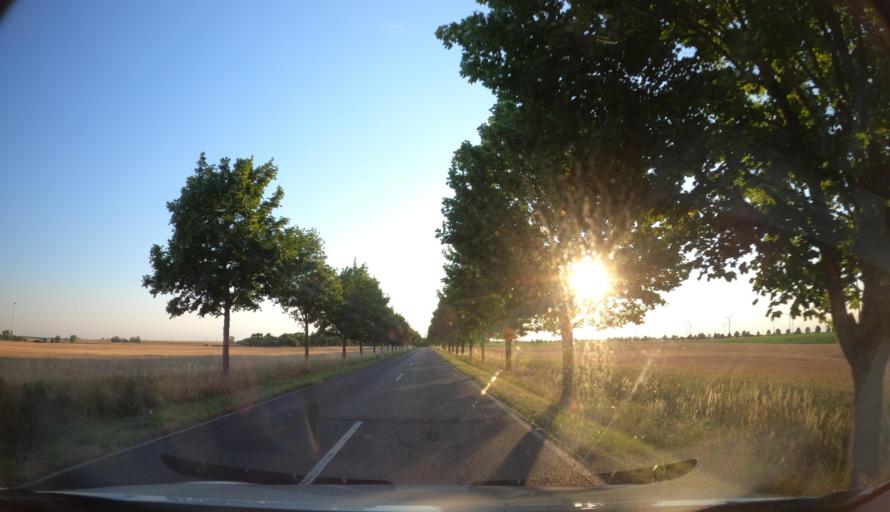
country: PL
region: West Pomeranian Voivodeship
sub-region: Powiat policki
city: Kolbaskowo
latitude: 53.3059
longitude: 14.4011
